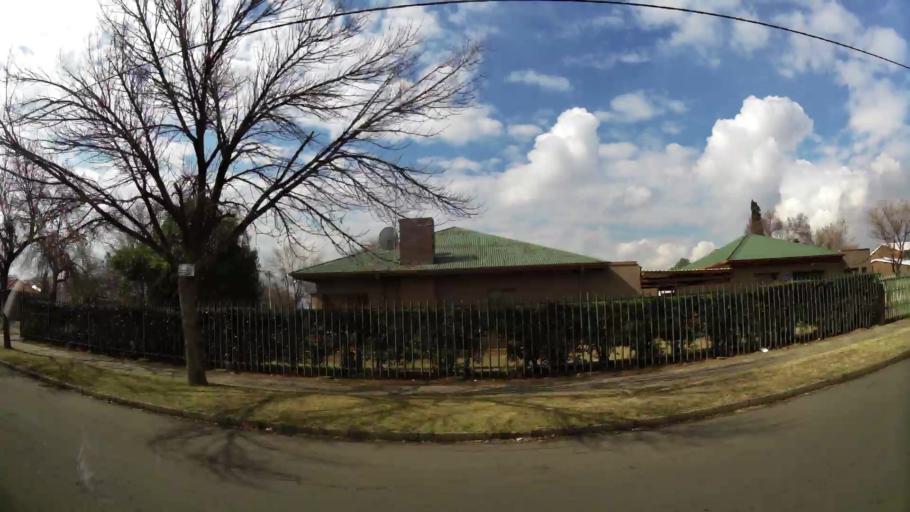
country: ZA
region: Gauteng
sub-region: Sedibeng District Municipality
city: Vereeniging
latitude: -26.6670
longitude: 27.9245
